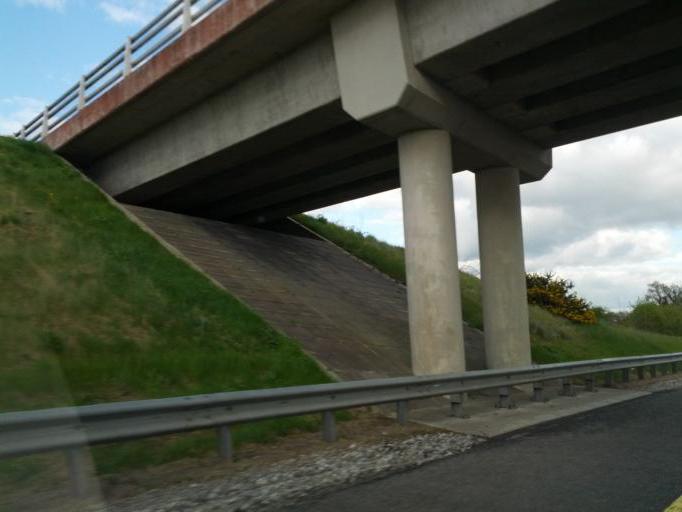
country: IE
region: Leinster
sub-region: Uibh Fhaili
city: Clara
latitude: 53.3799
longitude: -7.5656
